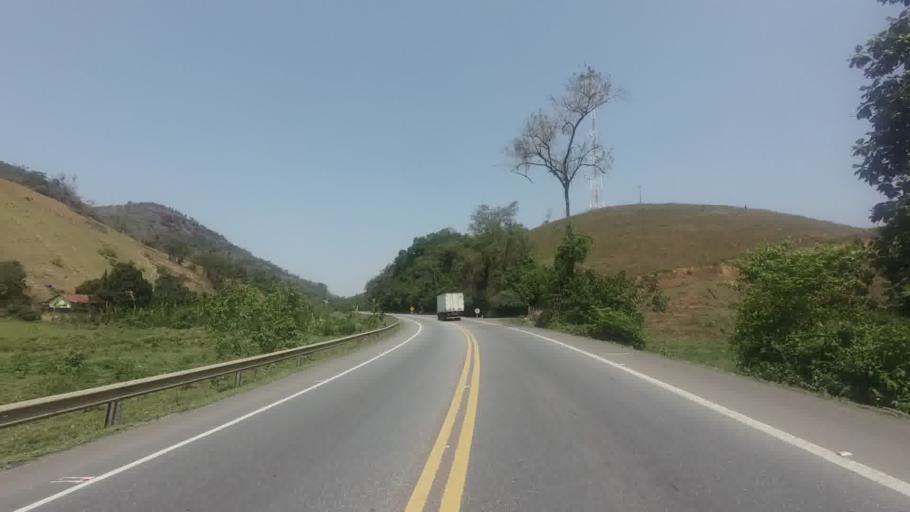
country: BR
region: Espirito Santo
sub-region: Rio Novo Do Sul
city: Rio Novo do Sul
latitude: -20.8392
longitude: -40.8710
